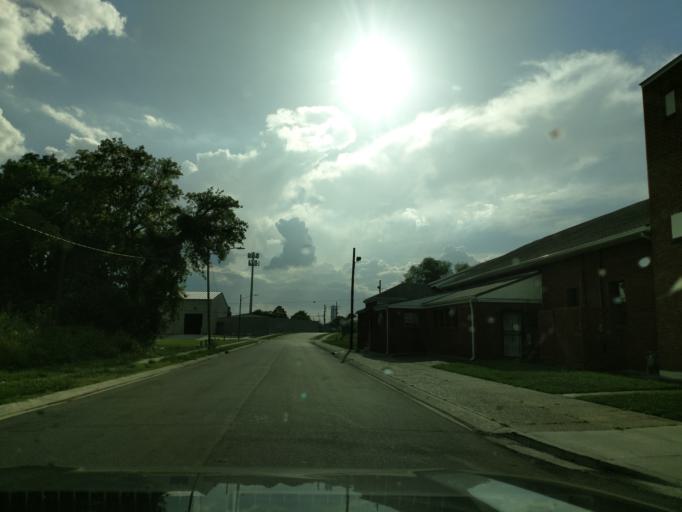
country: US
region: Louisiana
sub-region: Jefferson Parish
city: Gretna
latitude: 29.9418
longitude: -90.0424
